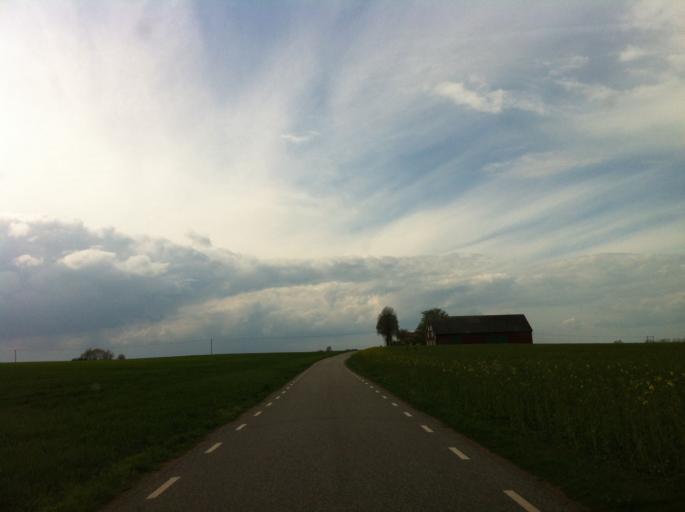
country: SE
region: Skane
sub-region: Svalovs Kommun
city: Teckomatorp
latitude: 55.8601
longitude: 13.0504
